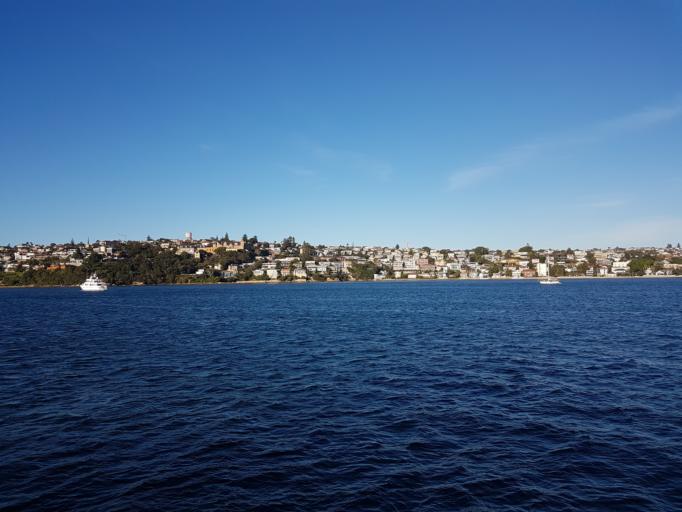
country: AU
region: New South Wales
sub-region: Woollahra
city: Point Piper
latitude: -33.8654
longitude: 151.2612
